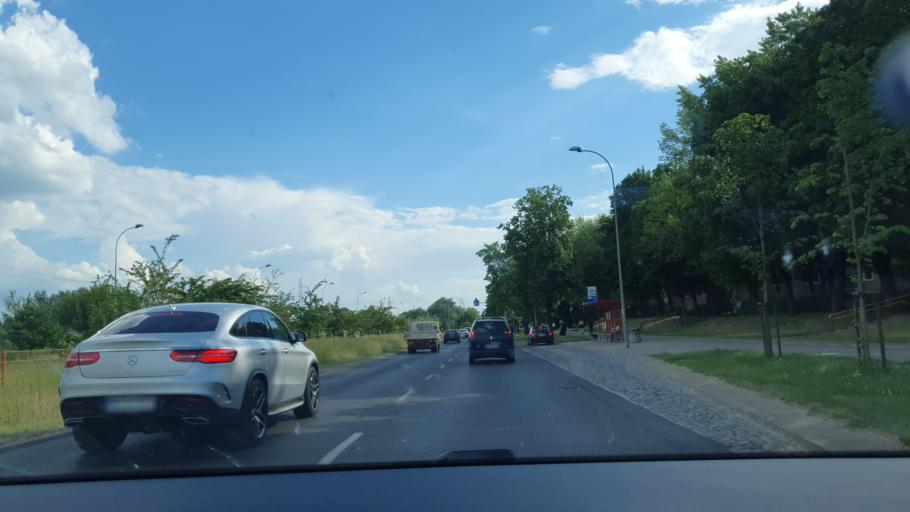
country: PL
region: Podlasie
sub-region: Bialystok
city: Bialystok
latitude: 53.1324
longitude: 23.1930
